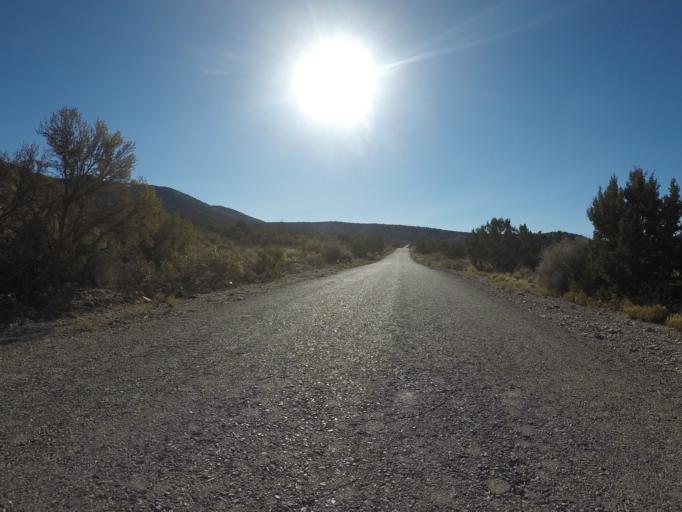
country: US
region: Nevada
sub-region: Clark County
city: Summerlin South
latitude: 36.0947
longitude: -115.5651
